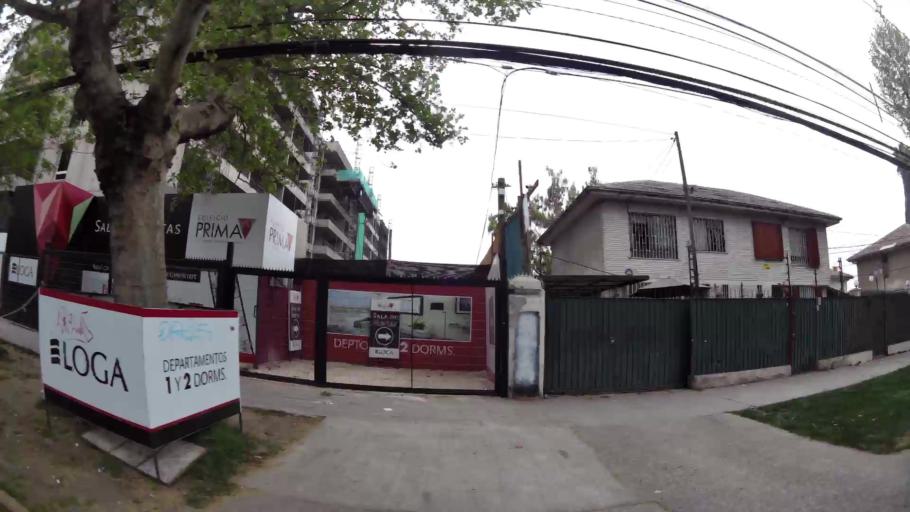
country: CL
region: Santiago Metropolitan
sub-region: Provincia de Santiago
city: Villa Presidente Frei, Nunoa, Santiago, Chile
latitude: -33.4674
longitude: -70.6005
